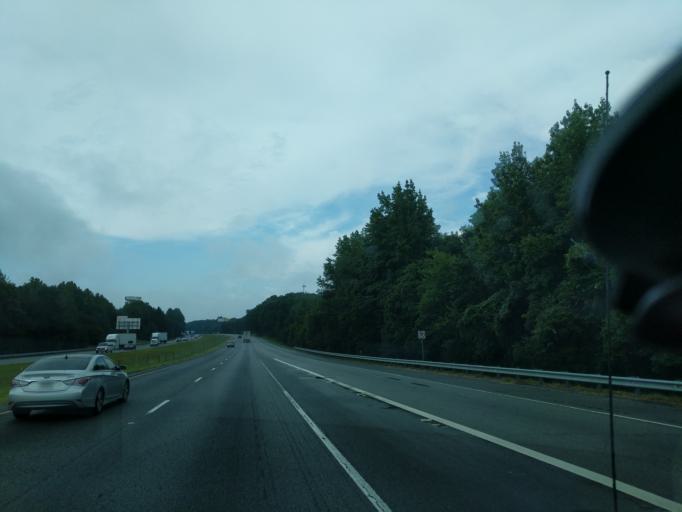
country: US
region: Georgia
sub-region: Franklin County
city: Carnesville
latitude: 34.3476
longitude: -83.3150
